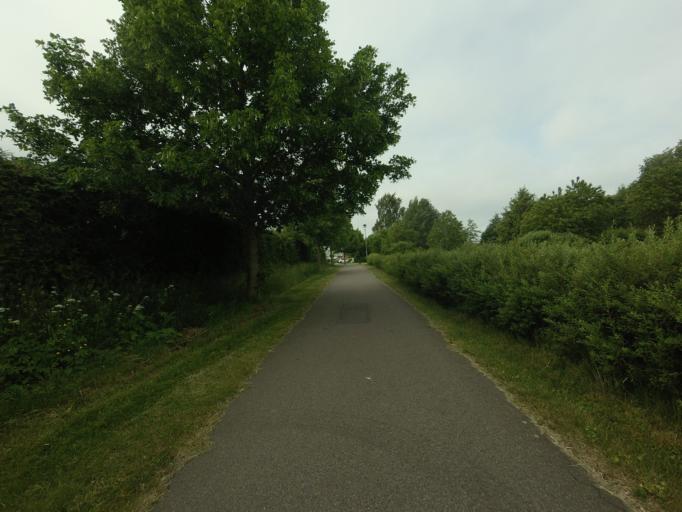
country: SE
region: Skane
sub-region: Bastads Kommun
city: Forslov
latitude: 56.3526
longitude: 12.8245
